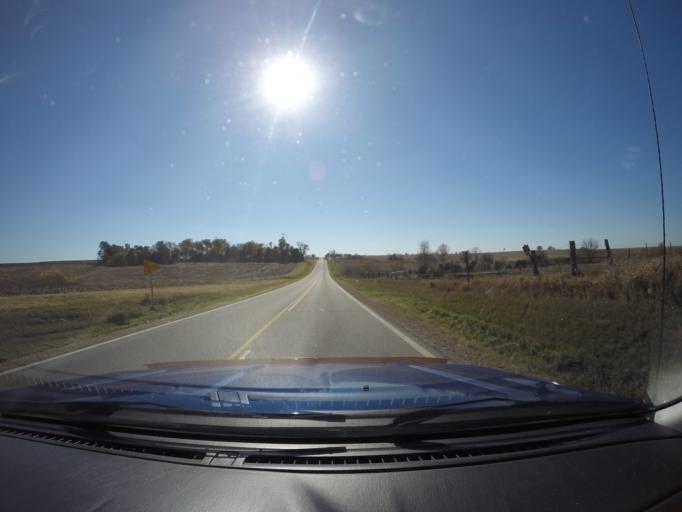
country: US
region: Kansas
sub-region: Marshall County
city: Marysville
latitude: 39.8488
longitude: -96.4171
